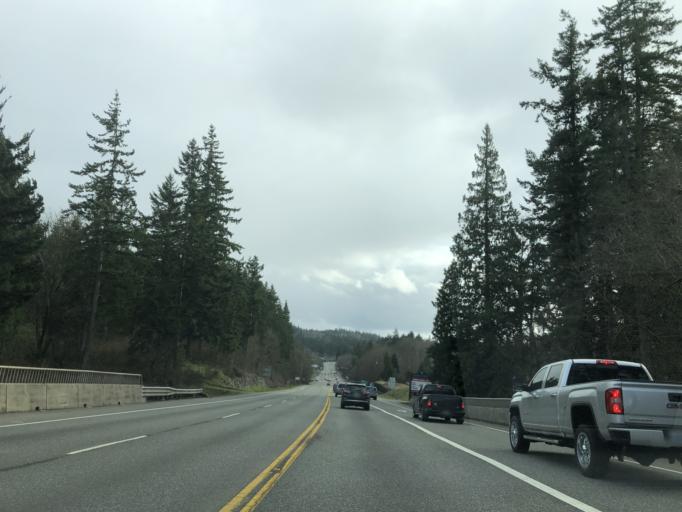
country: US
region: Washington
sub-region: Kitsap County
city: Poulsbo
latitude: 47.7554
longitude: -122.6503
